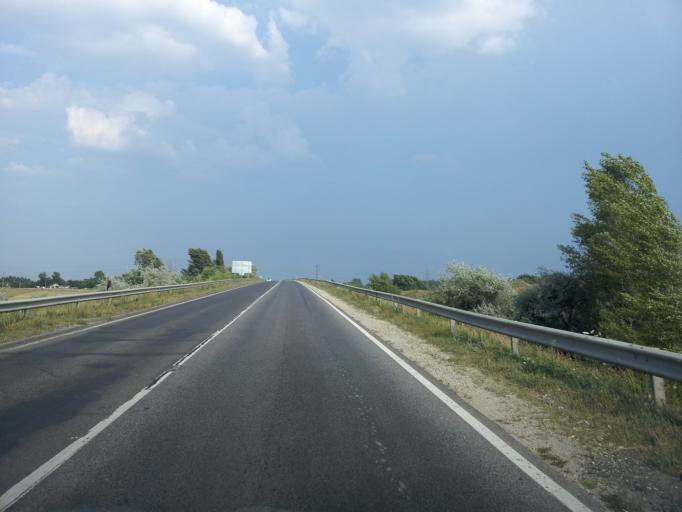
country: HU
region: Pest
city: Taksony
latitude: 47.3086
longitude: 19.0690
